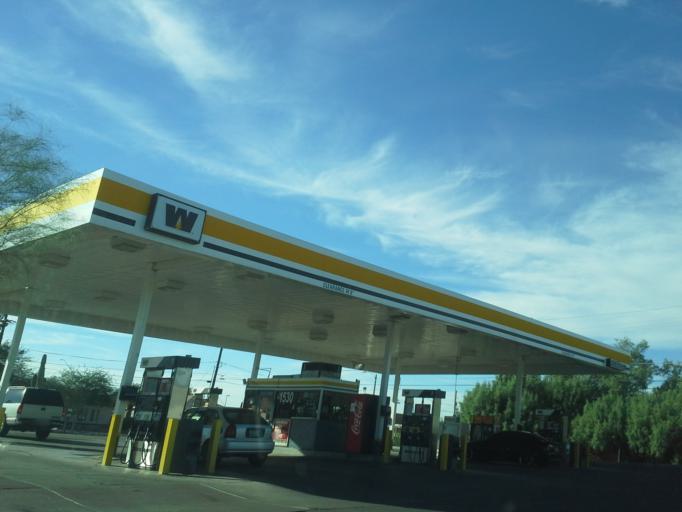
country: US
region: Arizona
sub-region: Pima County
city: South Tucson
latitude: 32.2290
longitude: -110.9978
